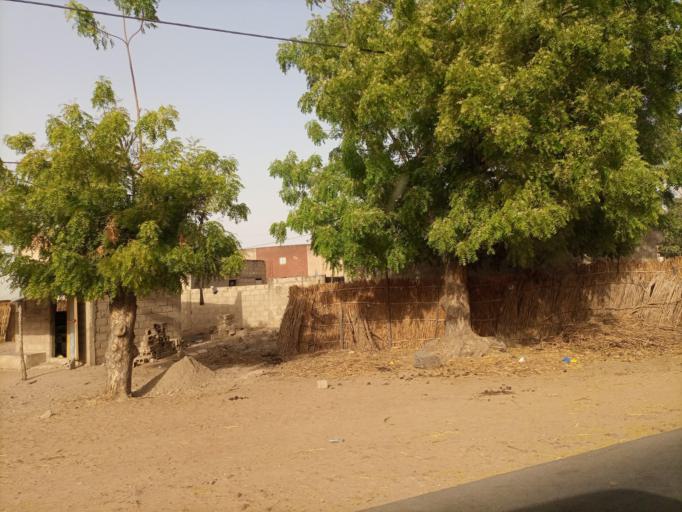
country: SN
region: Fatick
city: Passi
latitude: 14.0351
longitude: -16.3155
